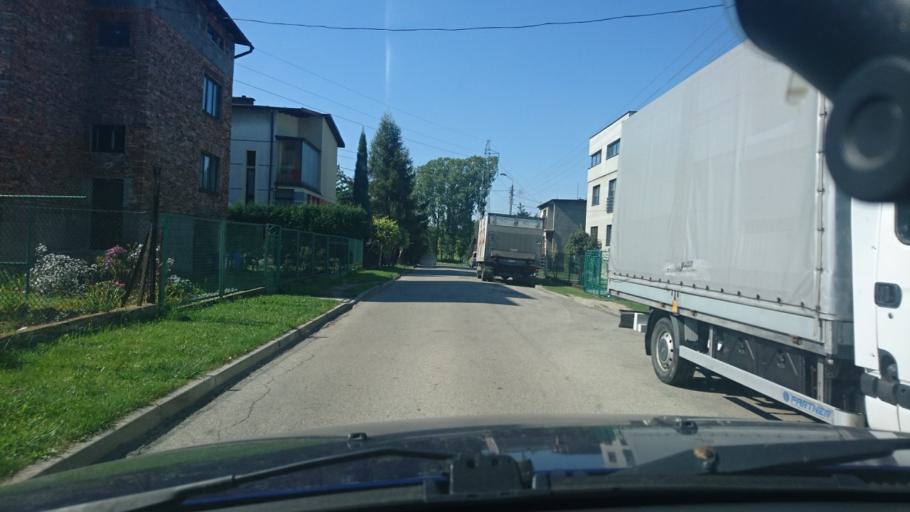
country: PL
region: Silesian Voivodeship
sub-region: Bielsko-Biala
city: Bielsko-Biala
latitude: 49.8431
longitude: 19.0640
